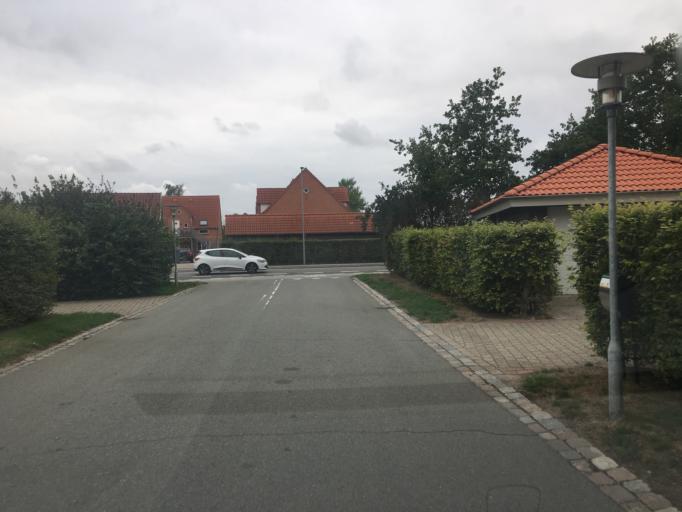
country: DK
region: South Denmark
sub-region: Tonder Kommune
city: Tonder
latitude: 54.9370
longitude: 8.8515
